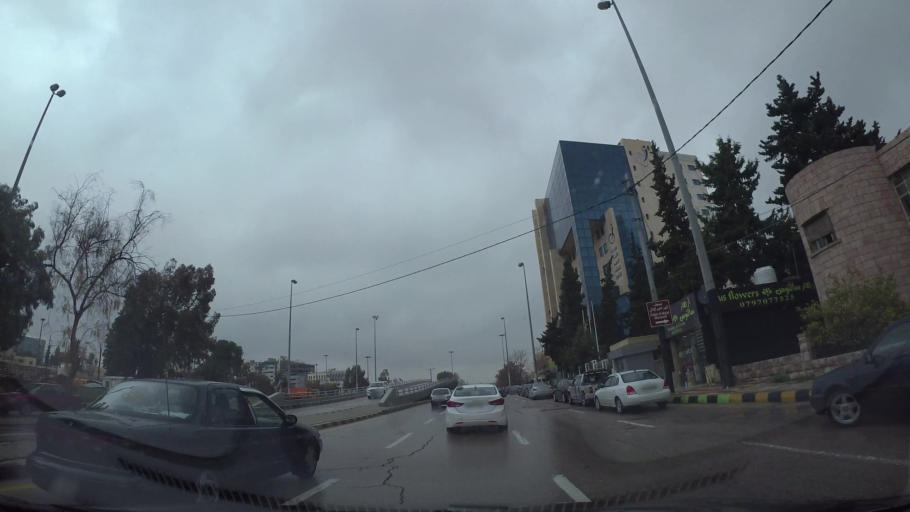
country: JO
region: Amman
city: Amman
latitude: 31.9710
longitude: 35.9094
